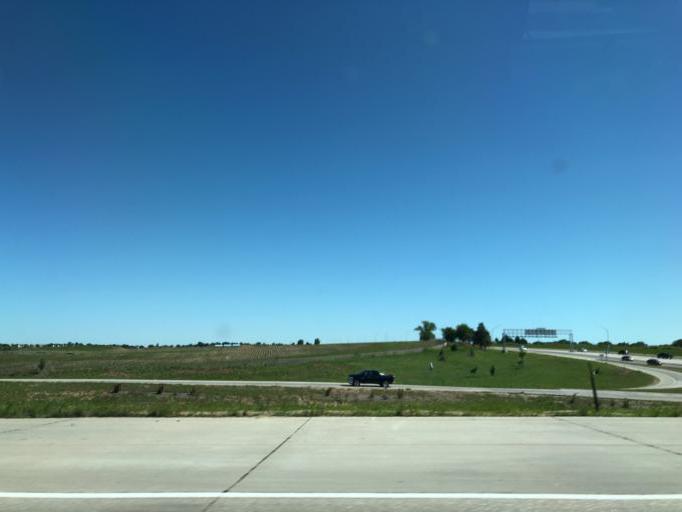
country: US
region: Nebraska
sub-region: Lancaster County
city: Lincoln
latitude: 40.8177
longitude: -96.7884
